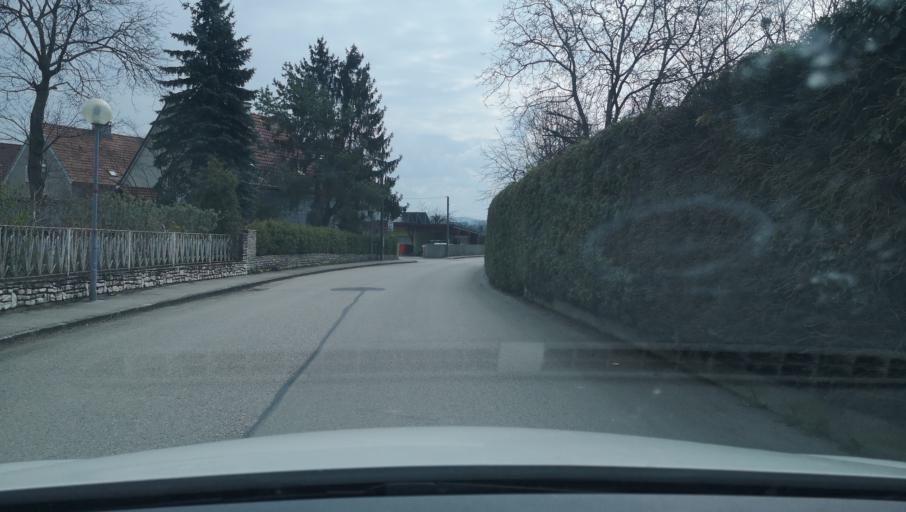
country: AT
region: Lower Austria
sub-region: Politischer Bezirk Amstetten
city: Amstetten
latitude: 48.1163
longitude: 14.8869
